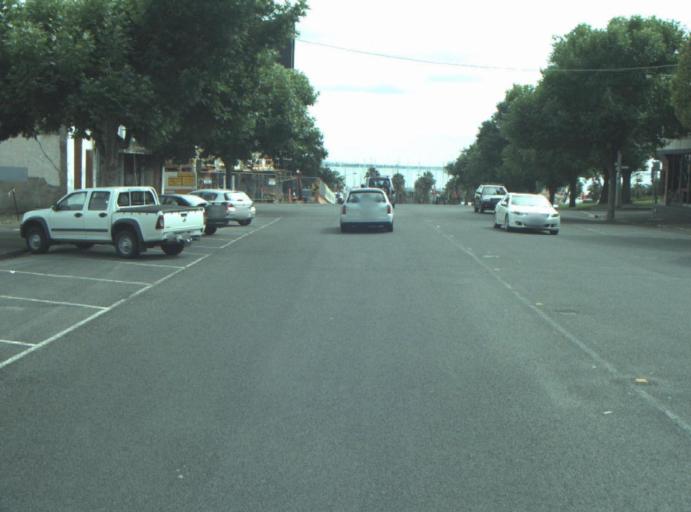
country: AU
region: Victoria
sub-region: Greater Geelong
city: Geelong
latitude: -38.1483
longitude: 144.3659
